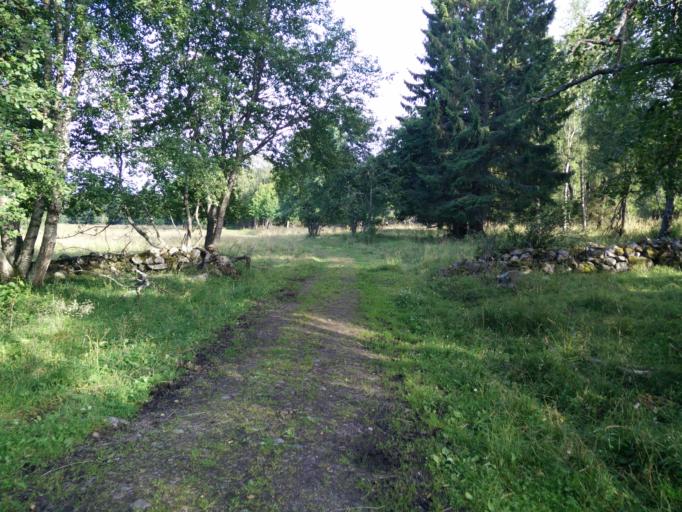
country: SE
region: Vaesternorrland
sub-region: Timra Kommun
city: Soraker
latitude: 62.4522
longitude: 17.4795
